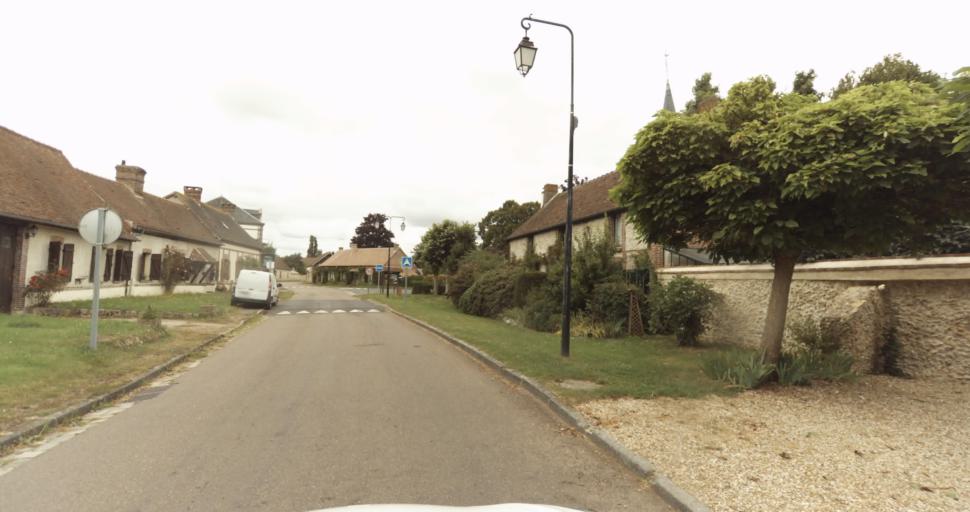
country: FR
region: Haute-Normandie
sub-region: Departement de l'Eure
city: La Madeleine-de-Nonancourt
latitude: 48.8335
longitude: 1.2021
